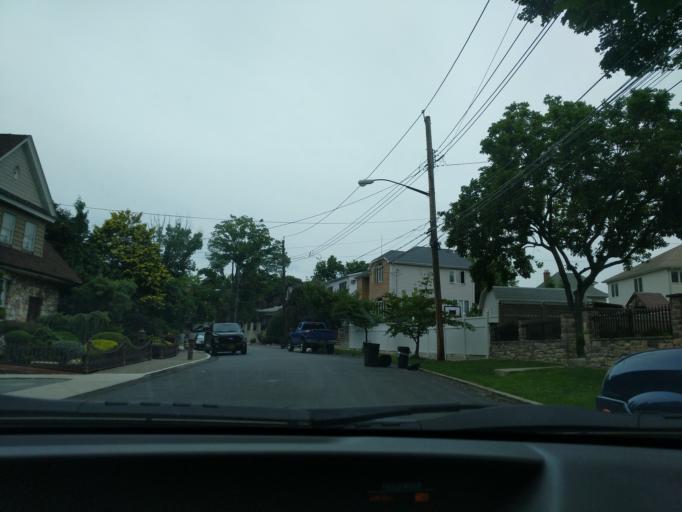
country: US
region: New York
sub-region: Richmond County
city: Staten Island
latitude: 40.5769
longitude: -74.1238
